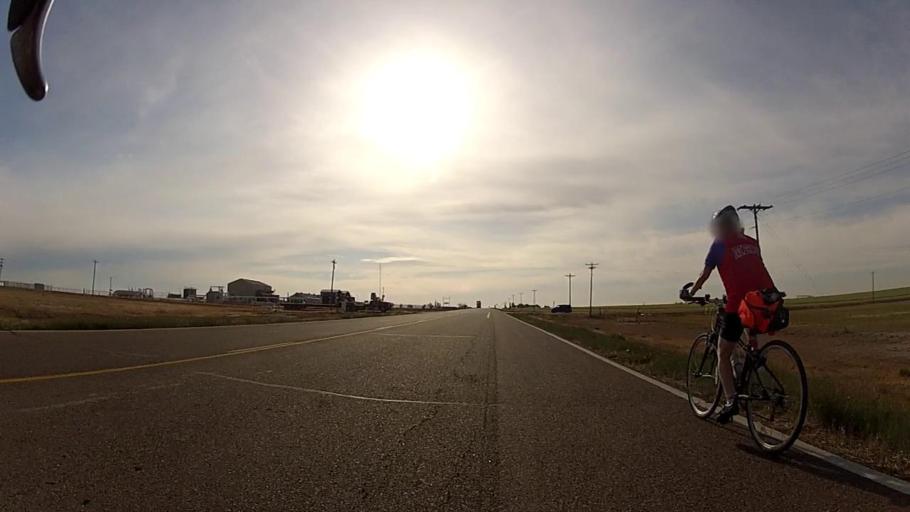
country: US
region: Kansas
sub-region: Grant County
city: Ulysses
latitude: 37.5766
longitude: -101.4911
